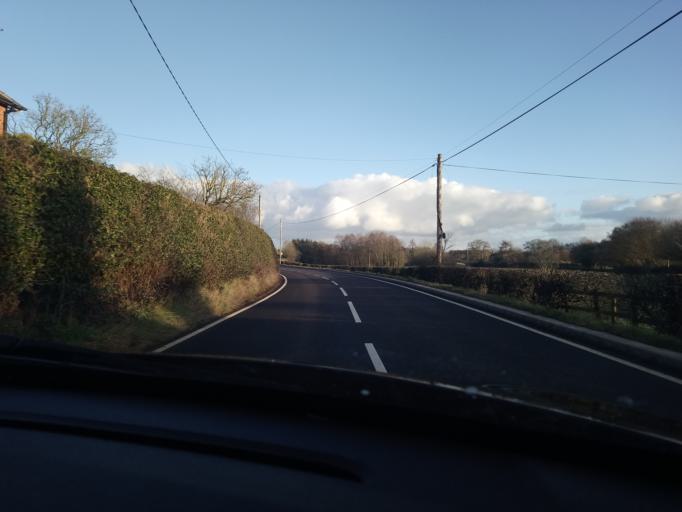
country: GB
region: England
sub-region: Shropshire
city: Ellesmere
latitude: 52.9077
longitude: -2.8310
